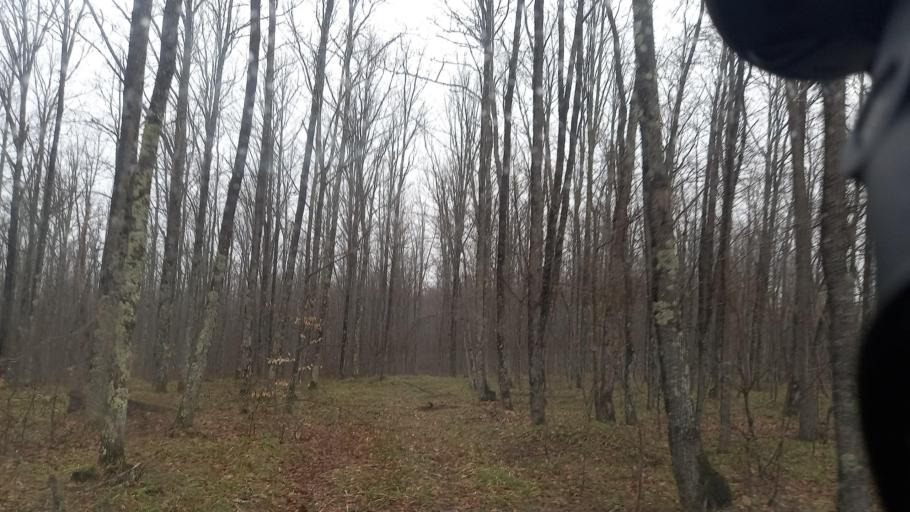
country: RU
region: Krasnodarskiy
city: Saratovskaya
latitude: 44.6197
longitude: 39.2543
